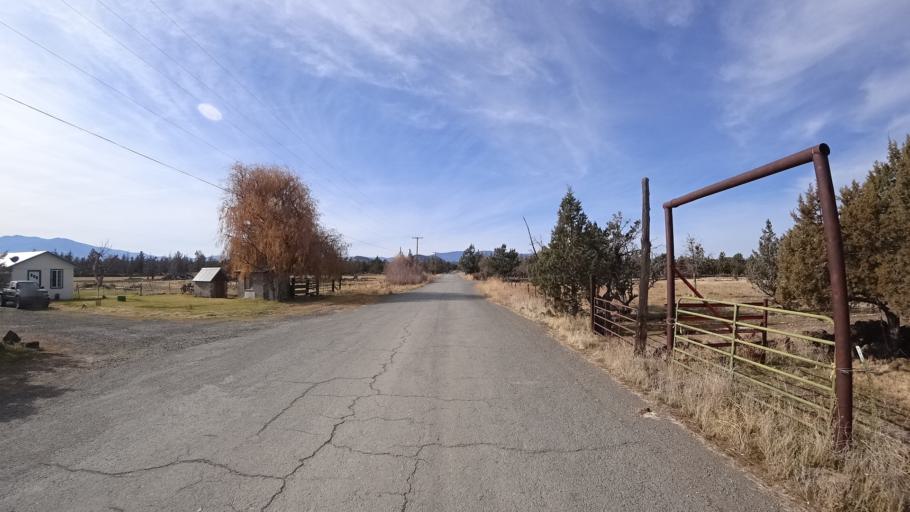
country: US
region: California
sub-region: Siskiyou County
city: Weed
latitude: 41.5955
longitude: -122.4091
